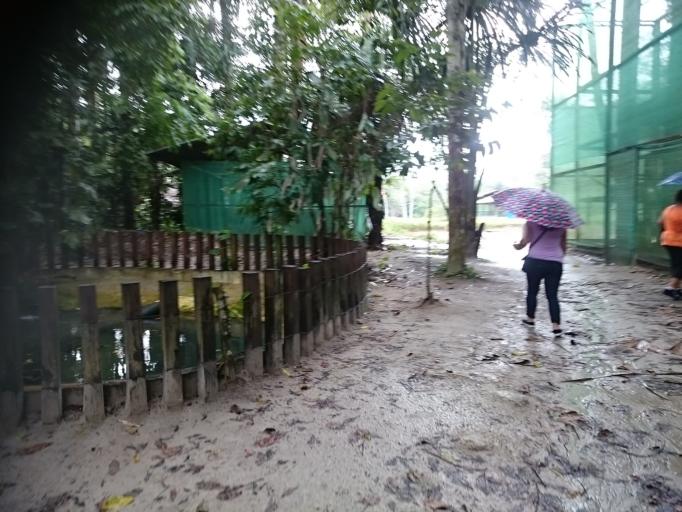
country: PE
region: Loreto
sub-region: Provincia de Maynas
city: Iquitos
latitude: -3.8177
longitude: -73.3223
